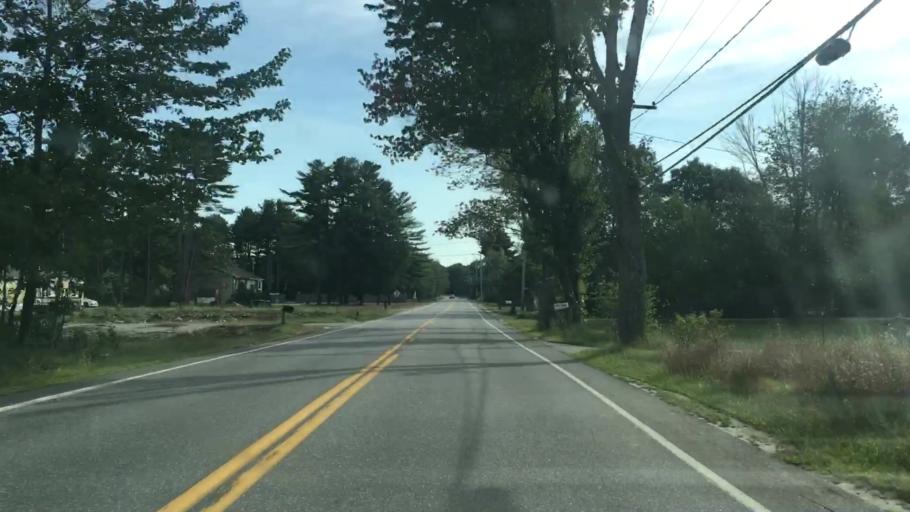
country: US
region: Maine
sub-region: Cumberland County
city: Brunswick
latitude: 43.9181
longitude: -69.9032
